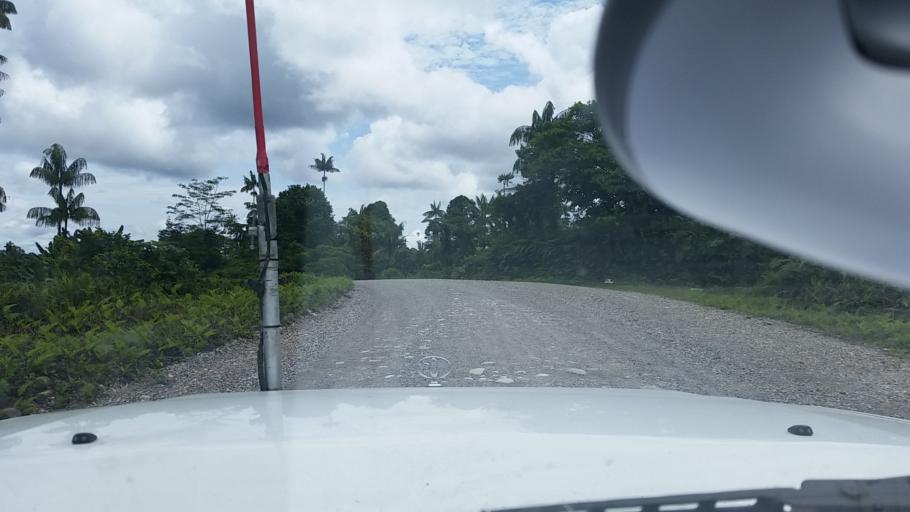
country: PG
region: Western Province
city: Kiunga
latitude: -5.6261
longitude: 141.2077
